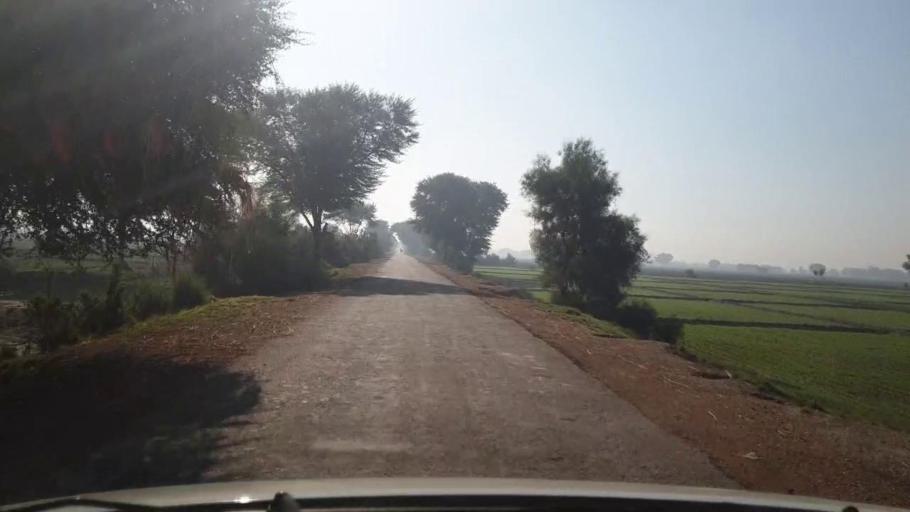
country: PK
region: Sindh
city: Dadu
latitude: 26.6654
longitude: 67.8172
